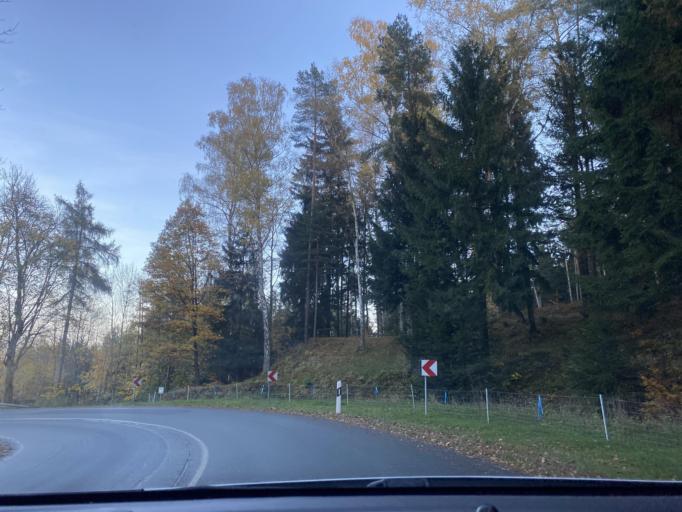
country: CZ
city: Hradek nad Nisou
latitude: 50.8397
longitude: 14.7985
